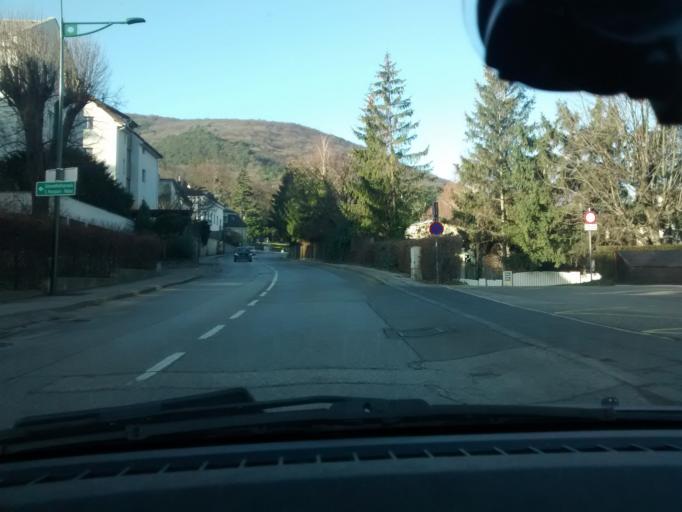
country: AT
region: Lower Austria
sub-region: Politischer Bezirk Modling
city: Hinterbruehl
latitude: 48.0810
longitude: 16.2639
